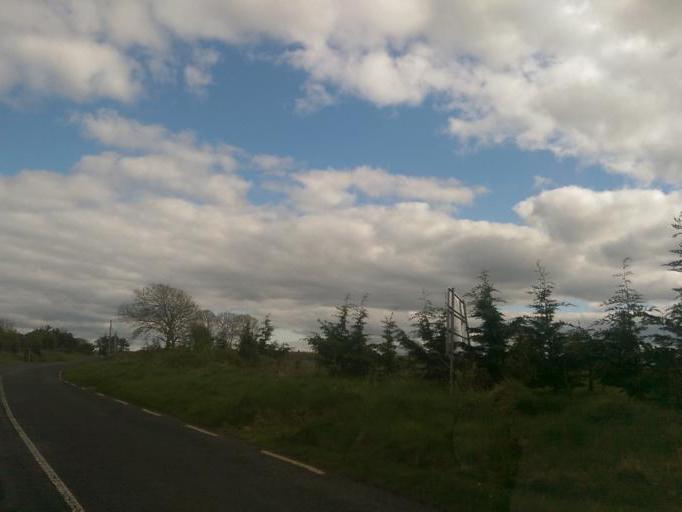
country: IE
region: Connaught
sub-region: County Galway
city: Loughrea
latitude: 53.4218
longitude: -8.5287
